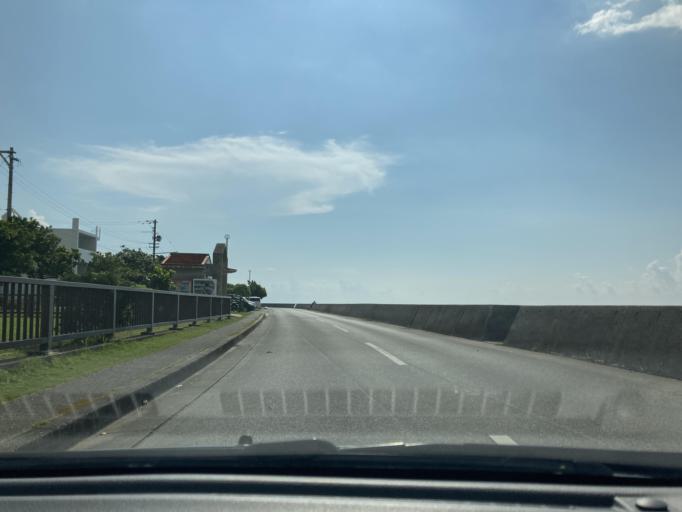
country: JP
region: Okinawa
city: Itoman
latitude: 26.1277
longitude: 127.7717
